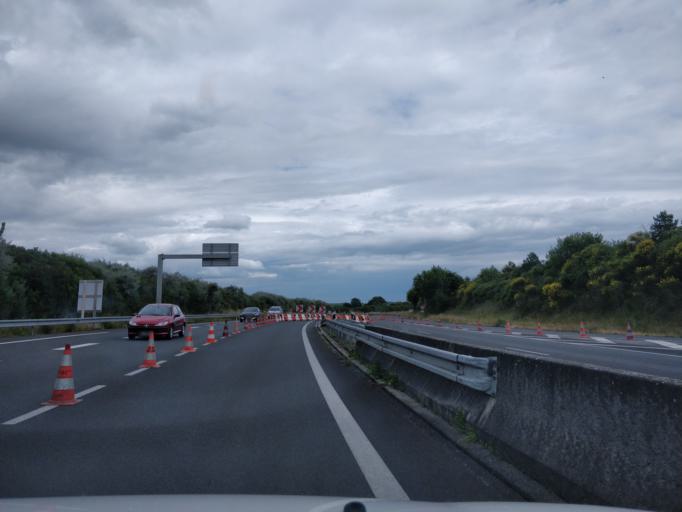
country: FR
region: Pays de la Loire
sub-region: Departement de Maine-et-Loire
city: Noyant-la-Gravoyere
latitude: 47.7088
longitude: -0.9722
